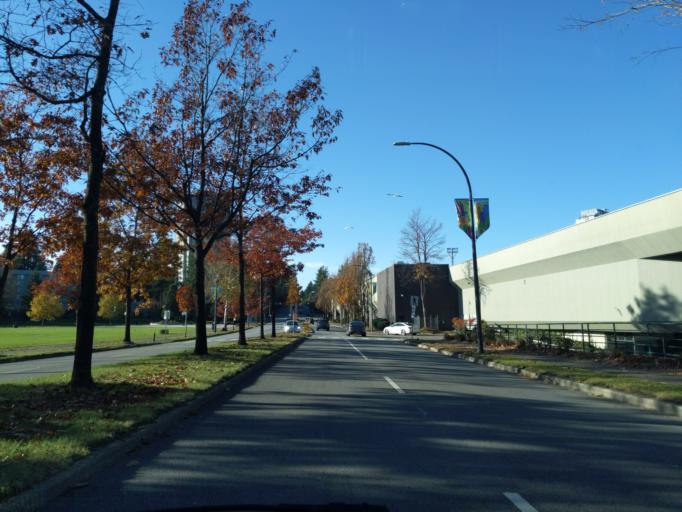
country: CA
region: British Columbia
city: New Westminster
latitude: 49.1850
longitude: -122.8488
